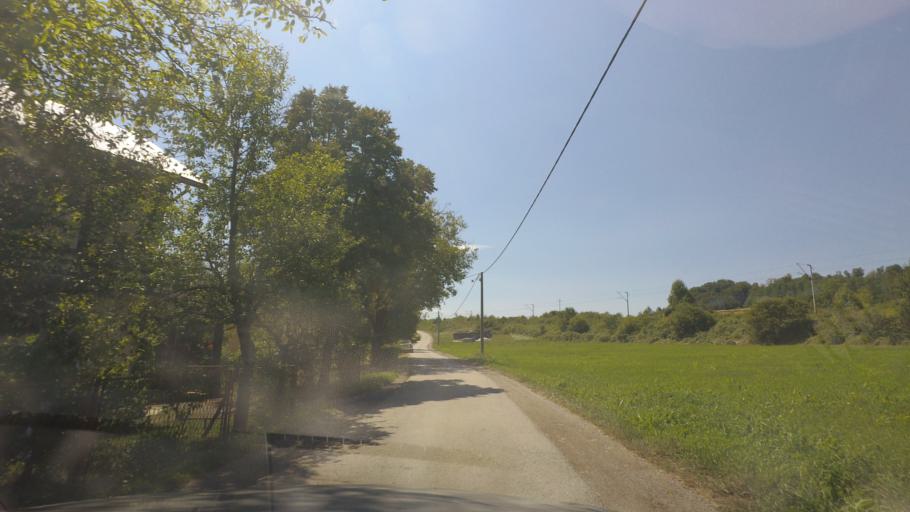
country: HR
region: Karlovacka
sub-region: Grad Karlovac
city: Karlovac
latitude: 45.4179
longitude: 15.4755
